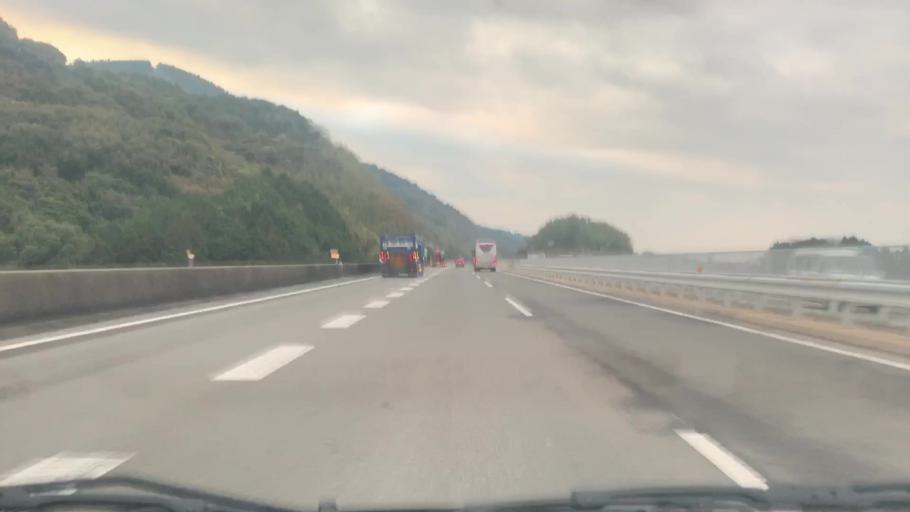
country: JP
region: Nagasaki
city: Omura
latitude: 32.9914
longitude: 129.9559
